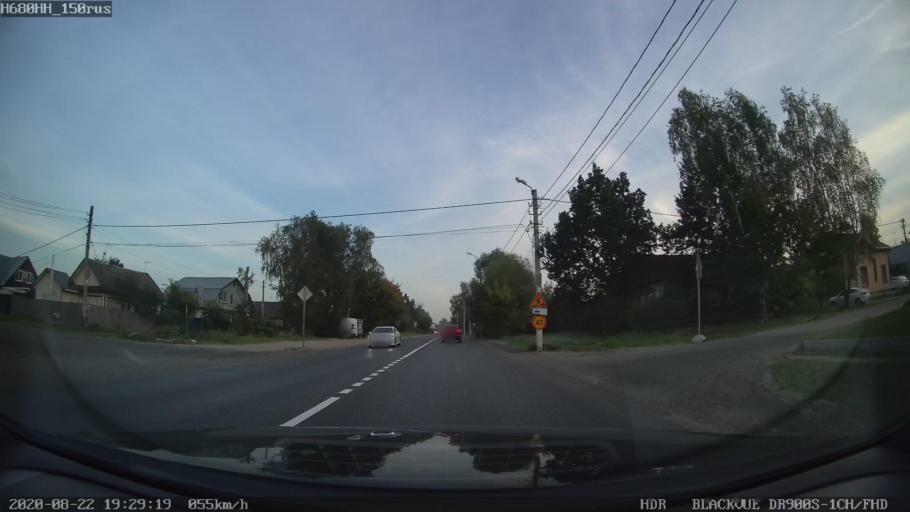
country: RU
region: Tverskaya
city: Tver
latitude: 56.8709
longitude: 35.9428
